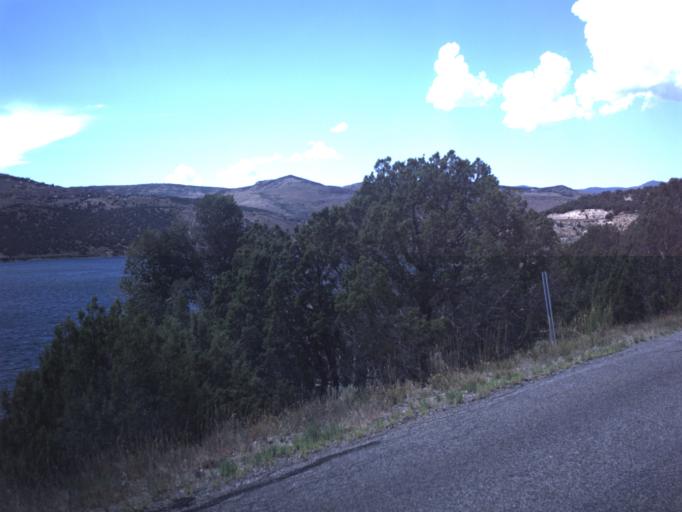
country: US
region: Utah
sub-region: Summit County
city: Oakley
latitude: 40.7615
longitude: -111.3775
